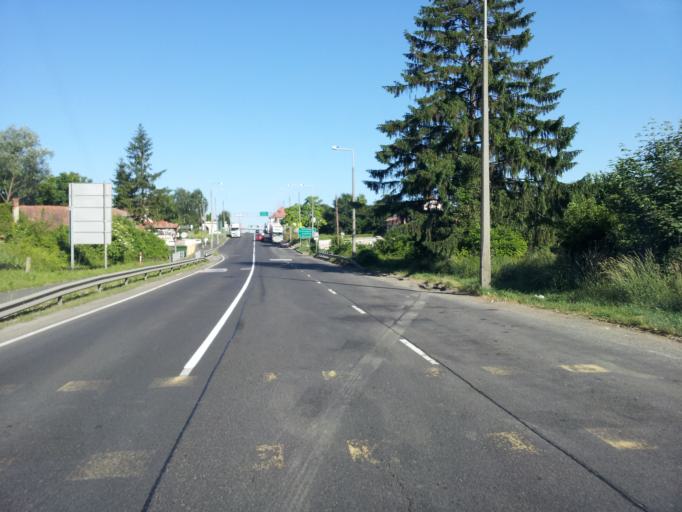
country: SK
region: Nitriansky
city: Sahy
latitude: 48.0565
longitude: 18.9693
